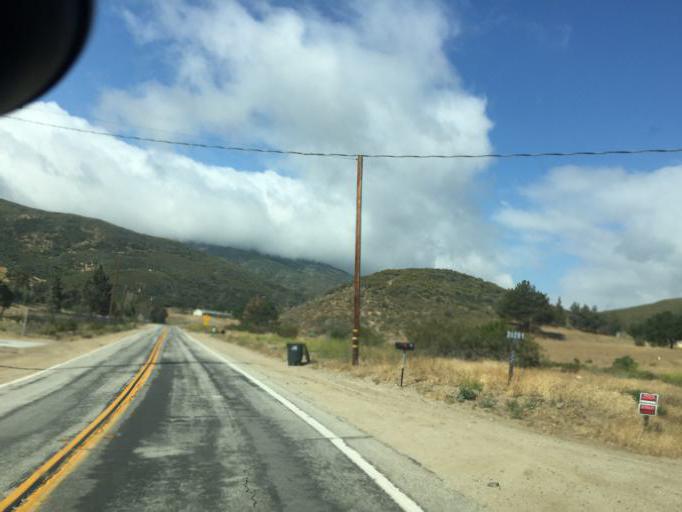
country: US
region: California
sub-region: Los Angeles County
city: Leona Valley
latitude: 34.5945
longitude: -118.2760
